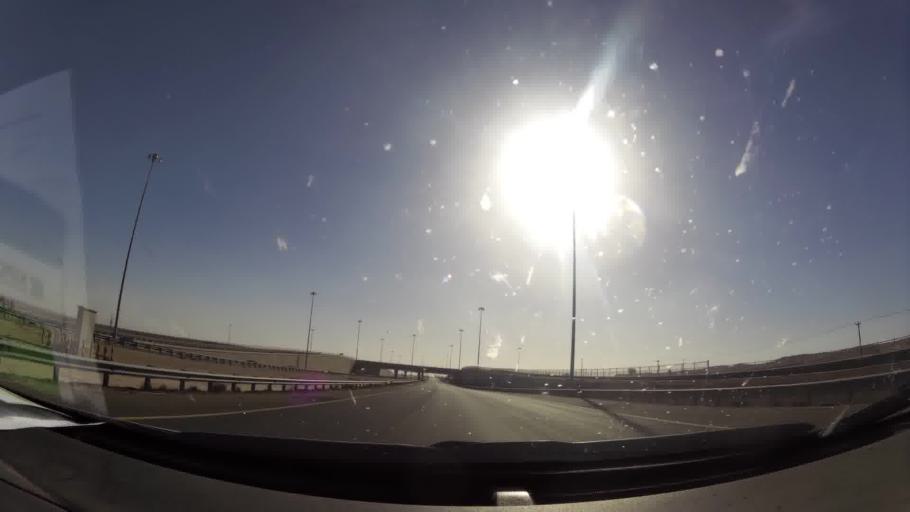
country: KW
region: Muhafazat al Jahra'
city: Al Jahra'
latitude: 29.4776
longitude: 47.7696
